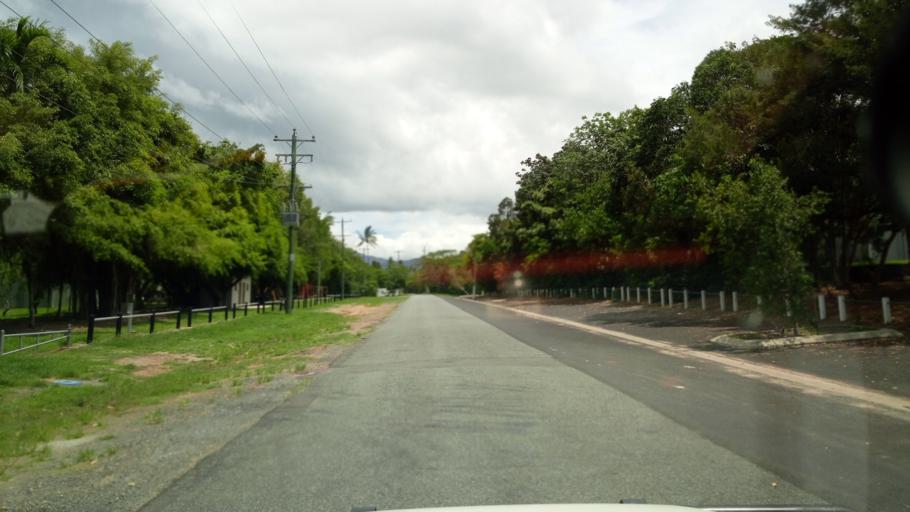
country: AU
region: Queensland
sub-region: Cairns
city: Yorkeys Knob
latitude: -16.8532
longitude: 145.7507
